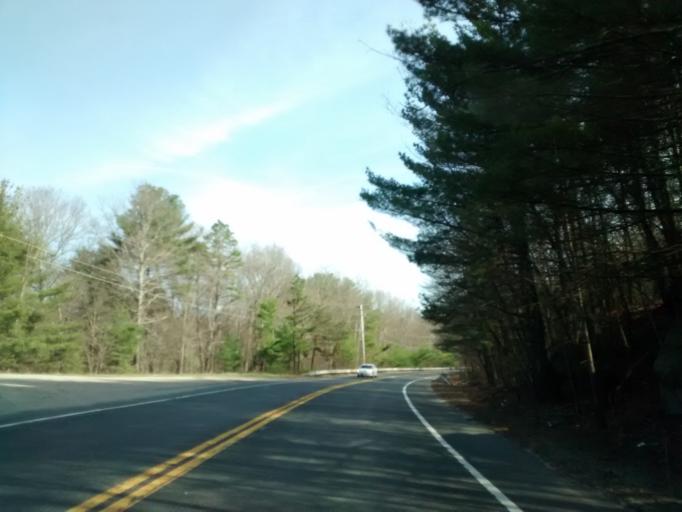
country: US
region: Massachusetts
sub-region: Worcester County
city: Whitinsville
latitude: 42.1152
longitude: -71.6382
